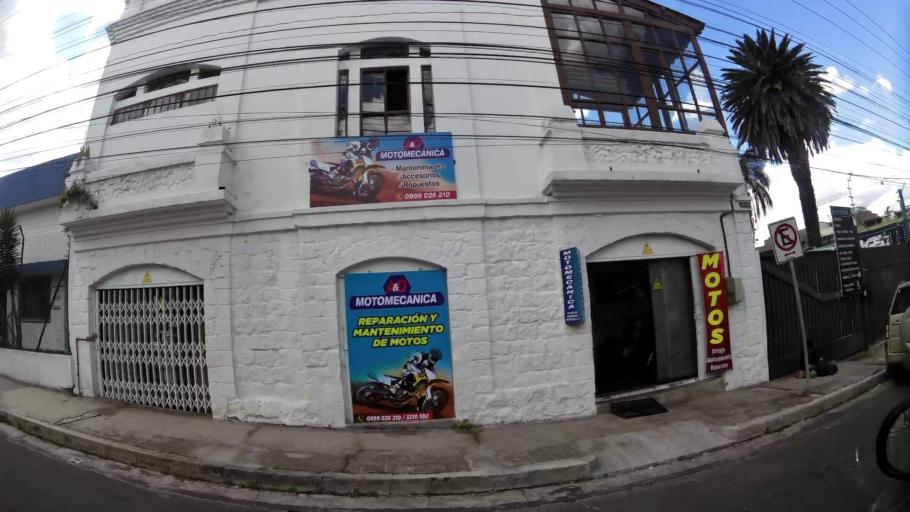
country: EC
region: Pichincha
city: Quito
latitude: -0.1936
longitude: -78.4946
